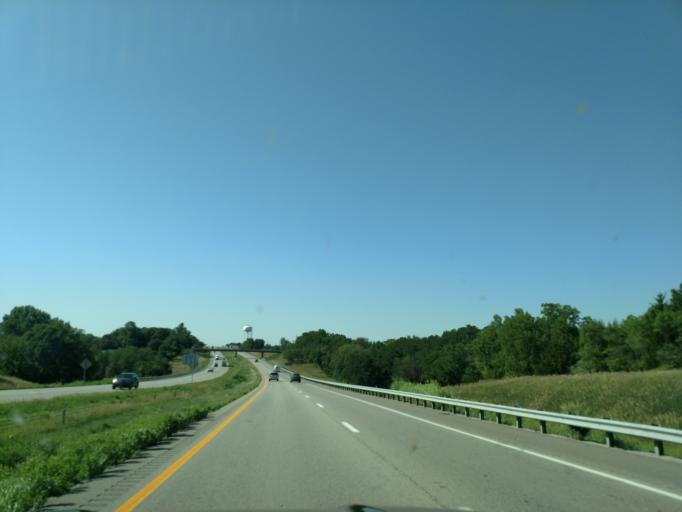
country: US
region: Missouri
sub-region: Andrew County
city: Country Club Village
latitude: 39.7882
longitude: -94.7953
